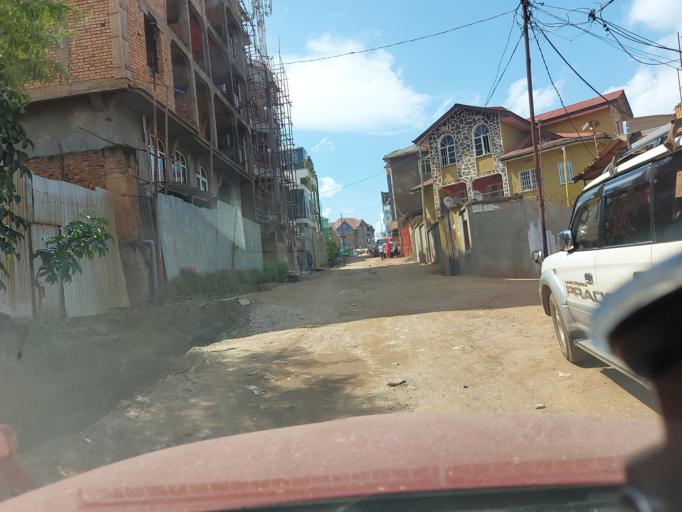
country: RW
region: Western Province
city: Cyangugu
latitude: -2.5008
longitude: 28.8796
